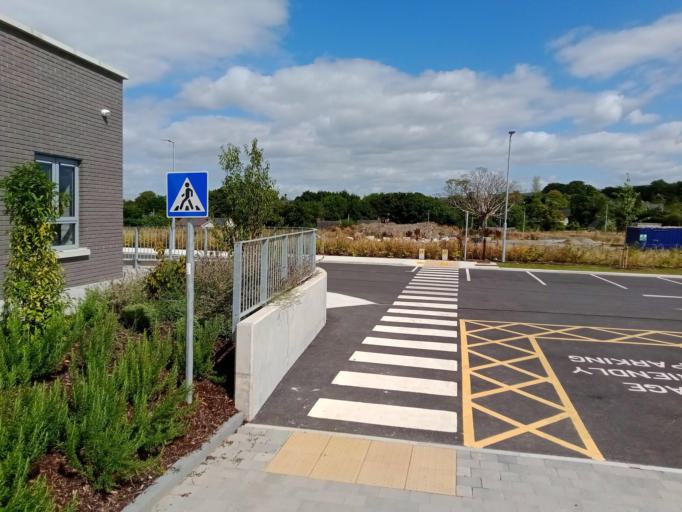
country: IE
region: Leinster
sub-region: Kilkenny
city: Thomastown
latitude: 52.5266
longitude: -7.1433
